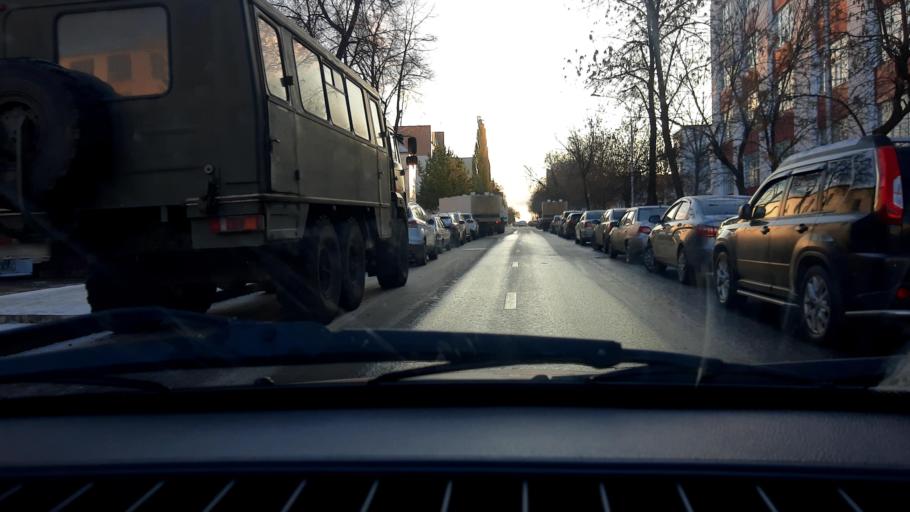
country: RU
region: Bashkortostan
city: Ufa
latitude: 54.7354
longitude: 55.9396
